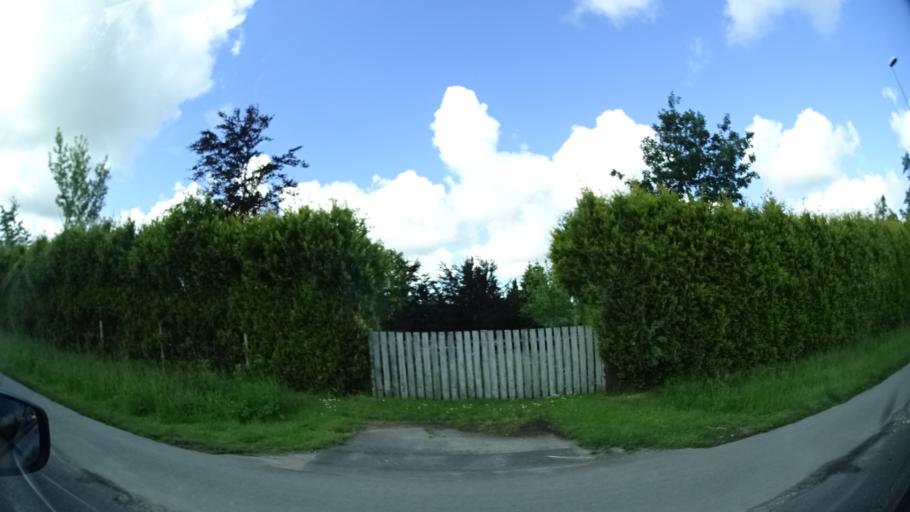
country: DK
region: Central Jutland
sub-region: Syddjurs Kommune
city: Ronde
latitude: 56.2863
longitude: 10.5829
